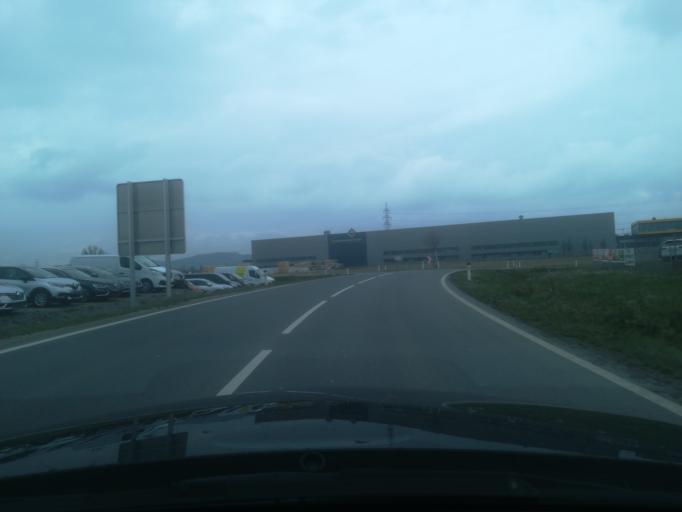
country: AT
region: Upper Austria
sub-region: Politischer Bezirk Urfahr-Umgebung
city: Feldkirchen an der Donau
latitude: 48.2988
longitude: 14.0150
